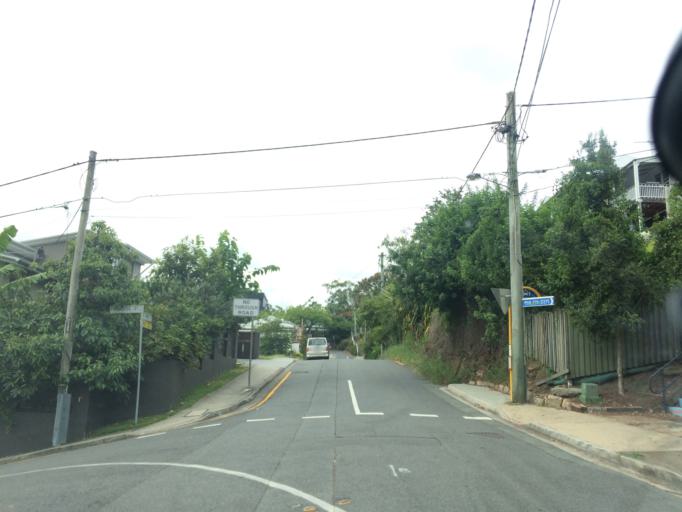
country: AU
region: Queensland
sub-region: Brisbane
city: South Brisbane
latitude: -27.4889
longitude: 153.0141
